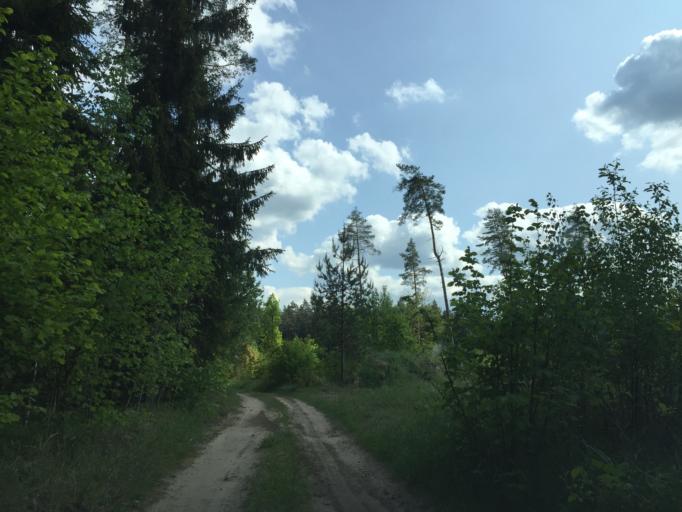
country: LV
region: Baldone
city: Baldone
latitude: 56.8045
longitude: 24.4247
